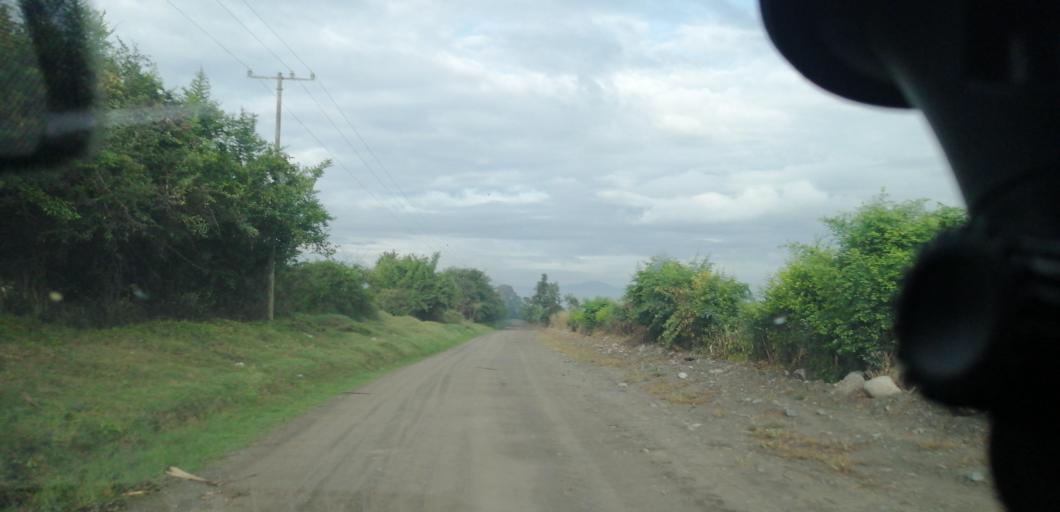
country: CO
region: Valle del Cauca
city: Palmira
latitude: 3.5544
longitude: -76.3677
